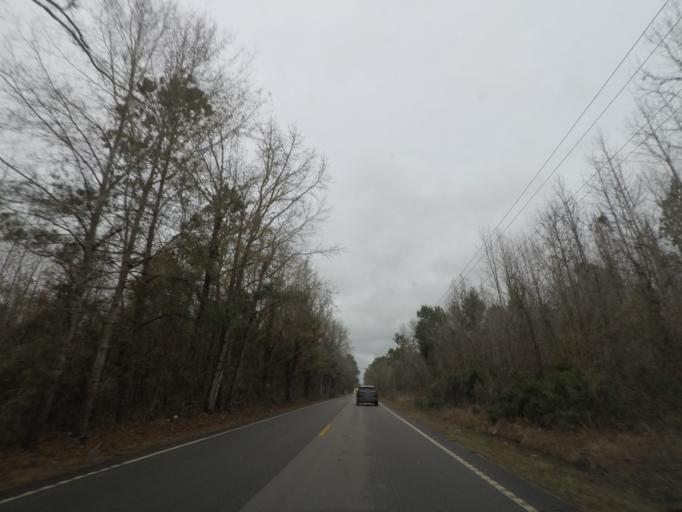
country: US
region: South Carolina
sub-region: Colleton County
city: Walterboro
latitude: 32.8564
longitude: -80.4902
